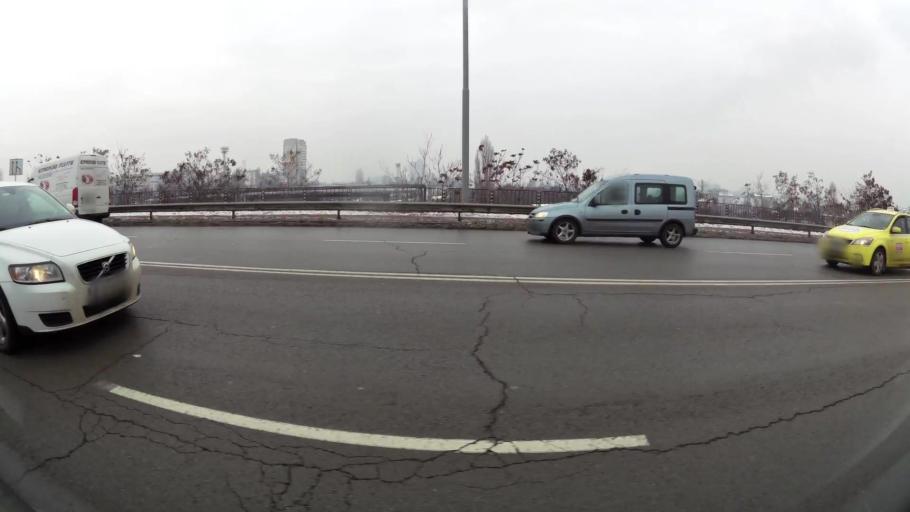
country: BG
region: Sofia-Capital
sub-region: Stolichna Obshtina
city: Sofia
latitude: 42.7177
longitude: 23.3100
